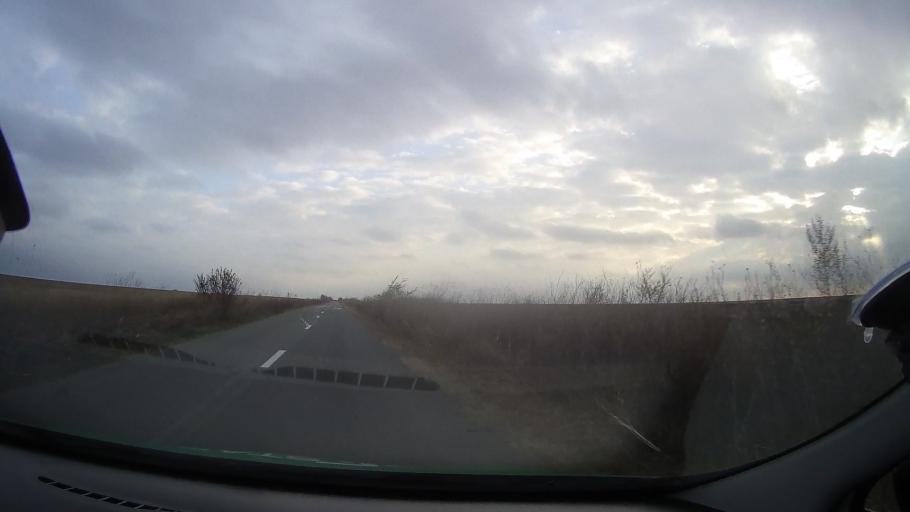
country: RO
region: Constanta
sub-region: Comuna Pestera
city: Pestera
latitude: 44.1402
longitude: 28.1173
